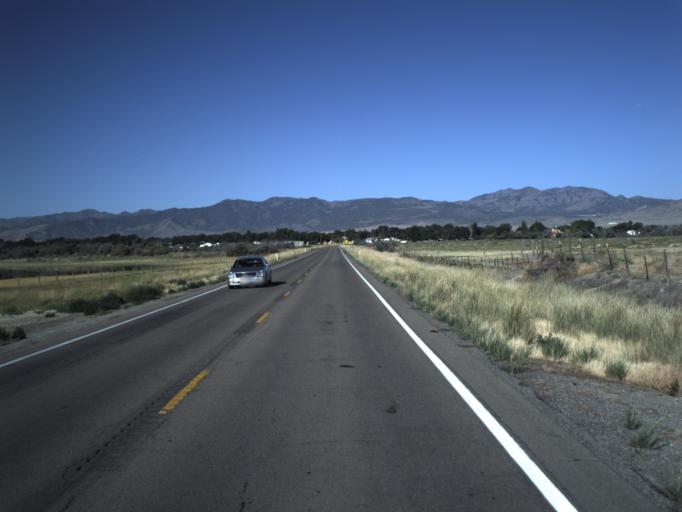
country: US
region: Utah
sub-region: Utah County
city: Genola
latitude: 39.9556
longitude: -111.8848
